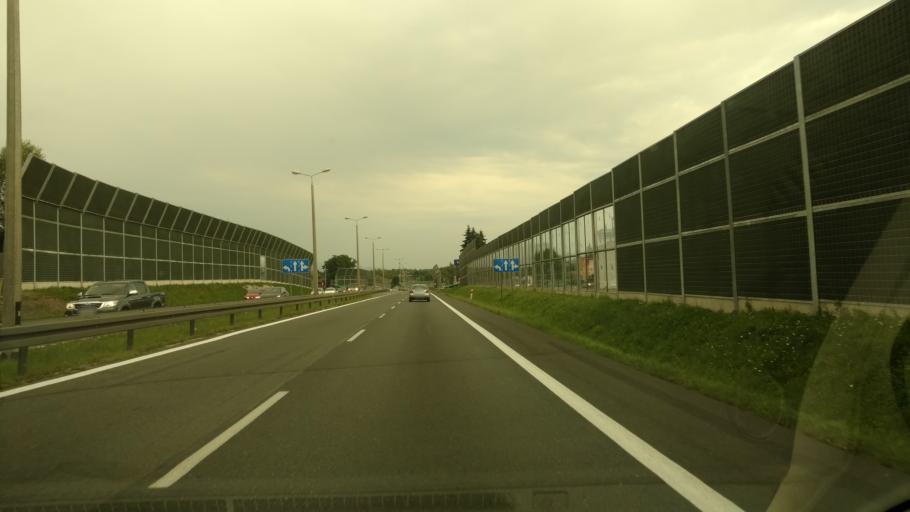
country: PL
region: Silesian Voivodeship
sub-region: Powiat pszczynski
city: Pszczyna
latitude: 49.9860
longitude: 18.9554
